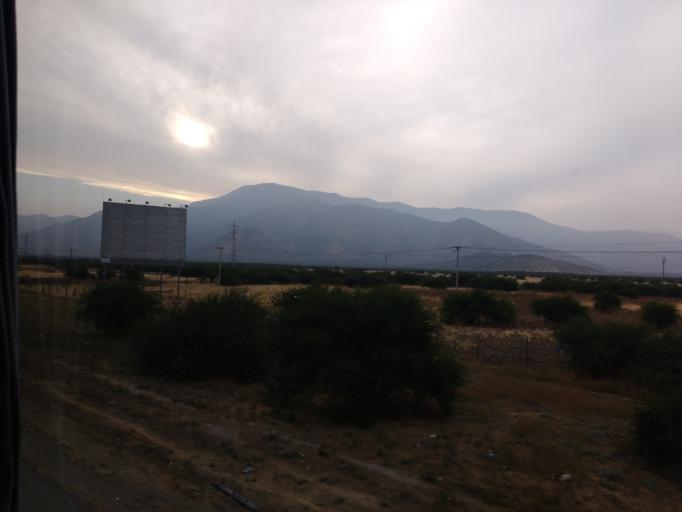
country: CL
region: Santiago Metropolitan
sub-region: Provincia de Santiago
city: Lo Prado
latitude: -33.4455
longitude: -70.8573
